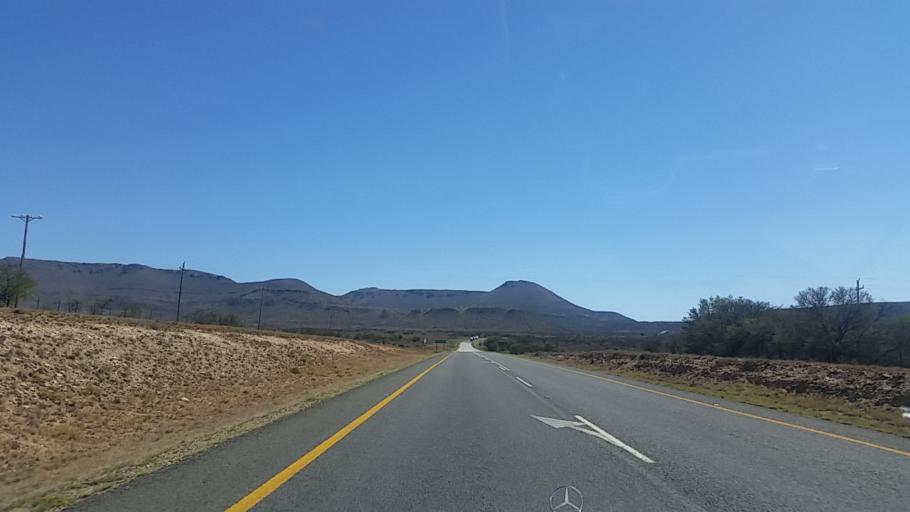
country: ZA
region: Eastern Cape
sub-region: Cacadu District Municipality
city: Graaff-Reinet
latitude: -32.0907
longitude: 24.6034
